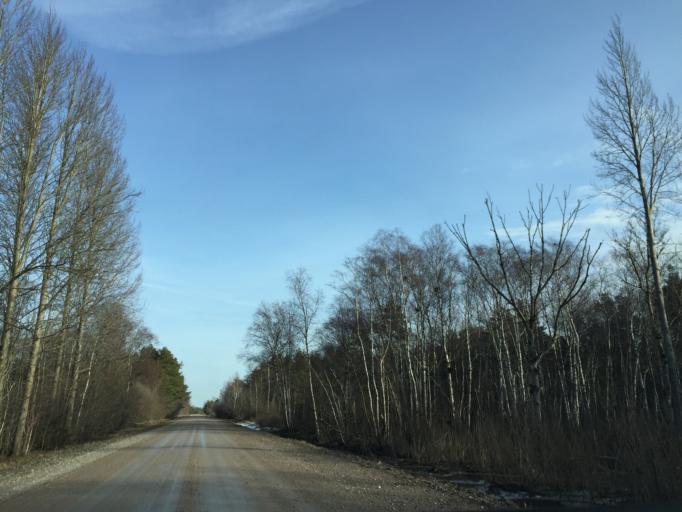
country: EE
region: Saare
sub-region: Kuressaare linn
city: Kuressaare
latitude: 58.3180
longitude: 21.9933
